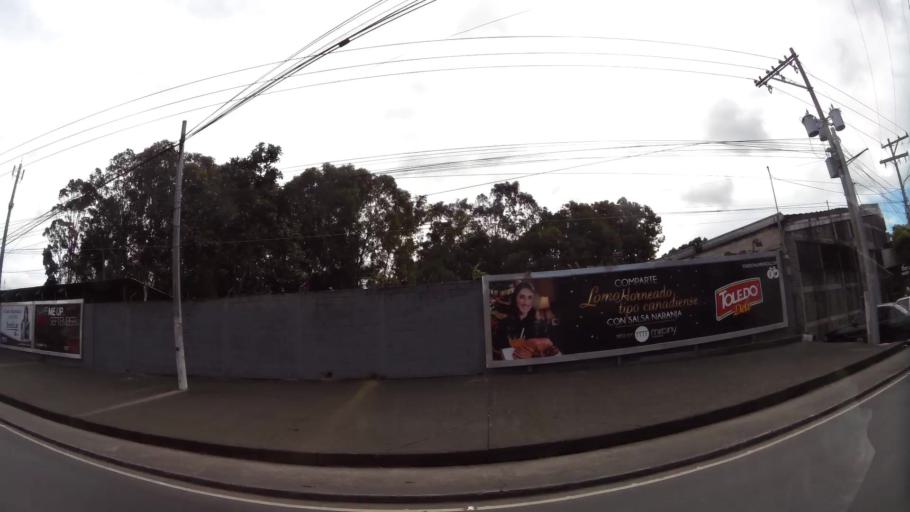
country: GT
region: Guatemala
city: Guatemala City
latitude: 14.6002
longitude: -90.5365
